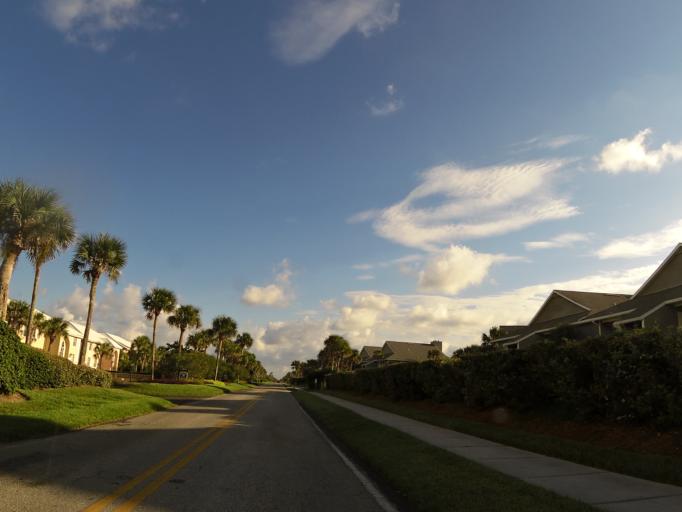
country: US
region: Florida
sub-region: Saint Johns County
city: Sawgrass
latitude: 30.2161
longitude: -81.3714
